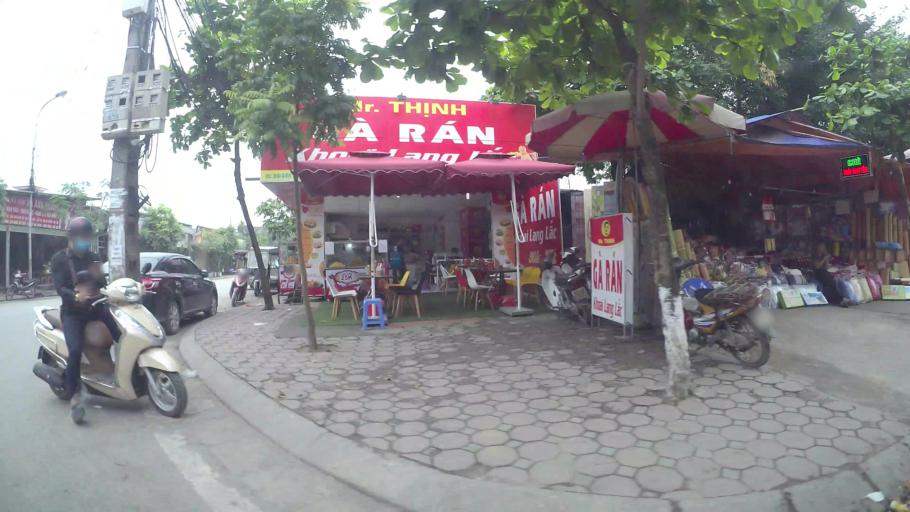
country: VN
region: Ha Noi
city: Hai BaTrung
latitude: 20.9843
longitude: 105.8732
